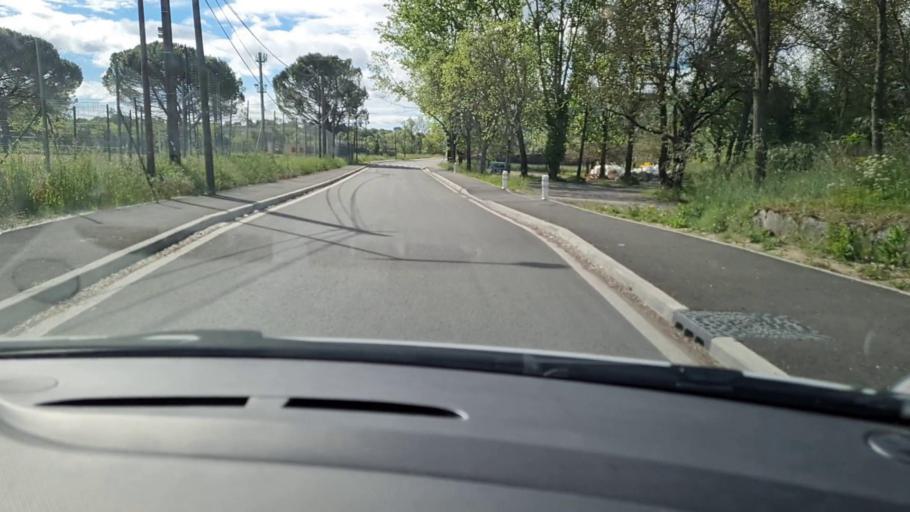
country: FR
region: Languedoc-Roussillon
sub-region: Departement du Gard
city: Sauve
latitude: 43.9460
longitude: 3.9490
